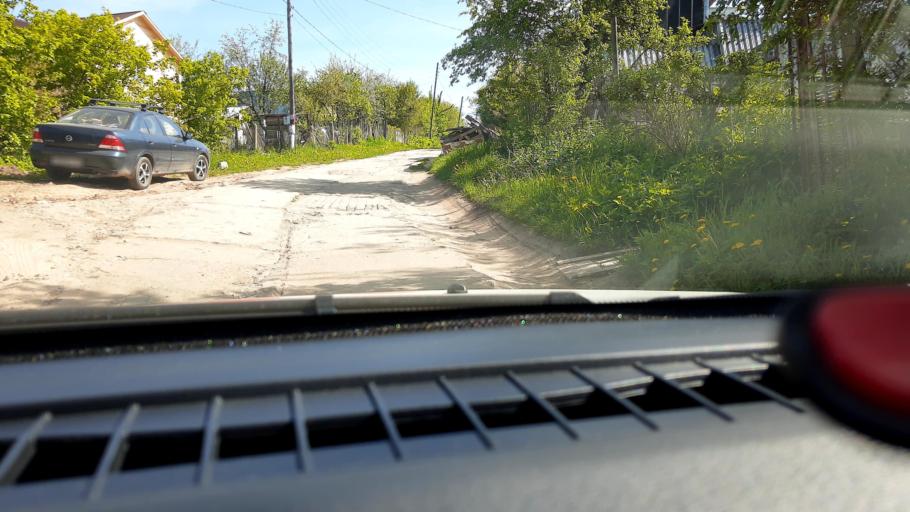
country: RU
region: Nizjnij Novgorod
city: Nizhniy Novgorod
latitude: 56.2301
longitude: 43.9642
